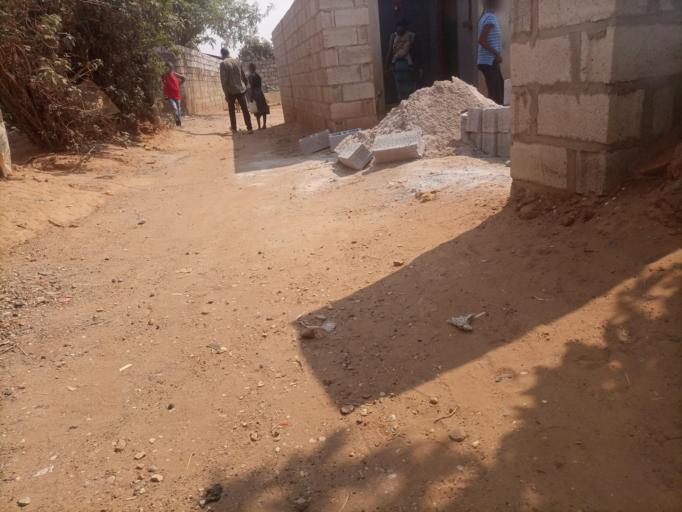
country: ZM
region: Lusaka
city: Lusaka
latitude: -15.4024
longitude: 28.3819
